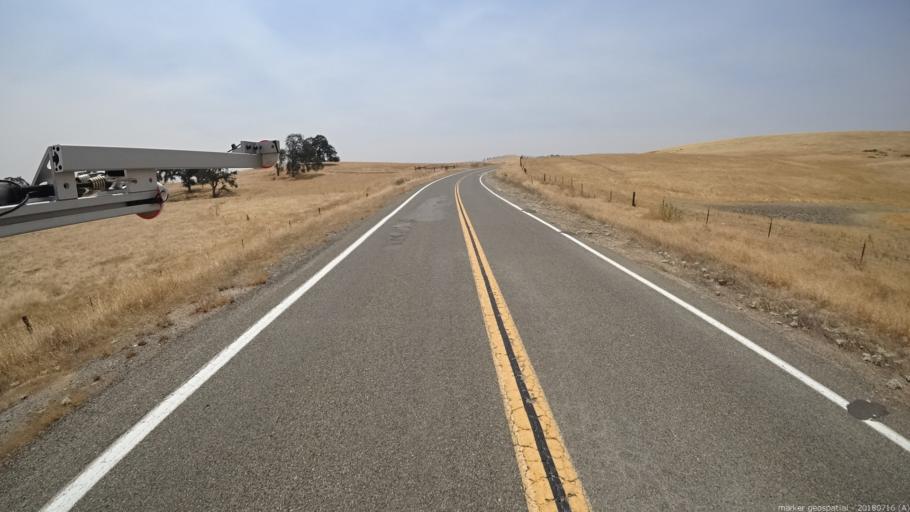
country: US
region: California
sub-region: Madera County
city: Bonadelle Ranchos-Madera Ranchos
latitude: 37.1323
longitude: -119.9182
